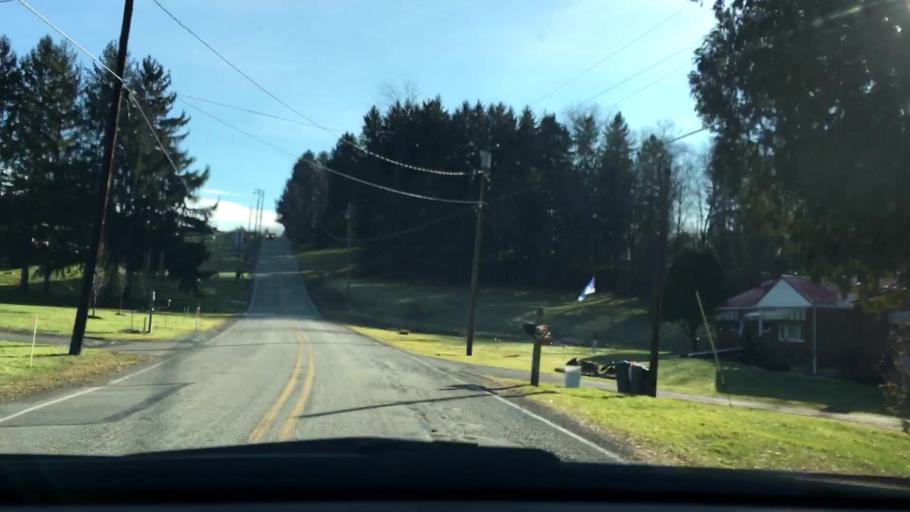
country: US
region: Pennsylvania
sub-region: Westmoreland County
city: Irwin
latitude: 40.3012
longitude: -79.7004
